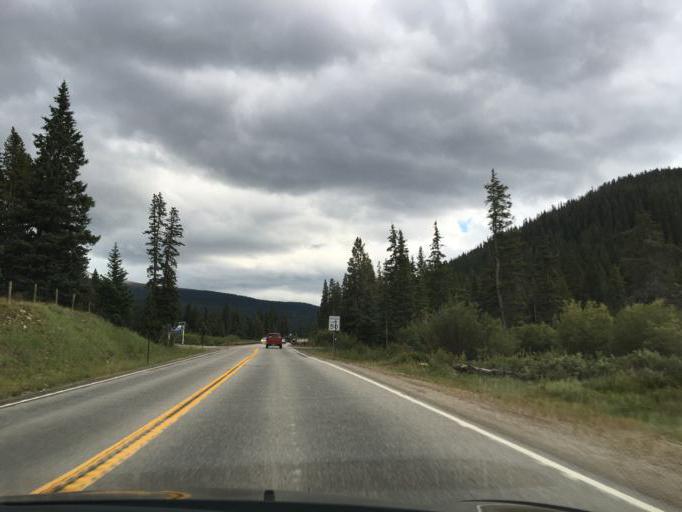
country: US
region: Colorado
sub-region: Summit County
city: Breckenridge
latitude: 39.4032
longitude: -106.0501
